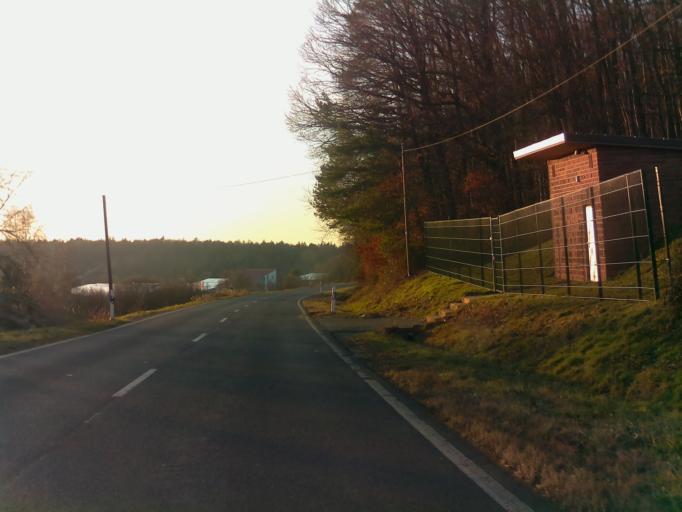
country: DE
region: Bavaria
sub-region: Regierungsbezirk Unterfranken
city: Geiselbach
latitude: 50.1278
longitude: 9.2046
